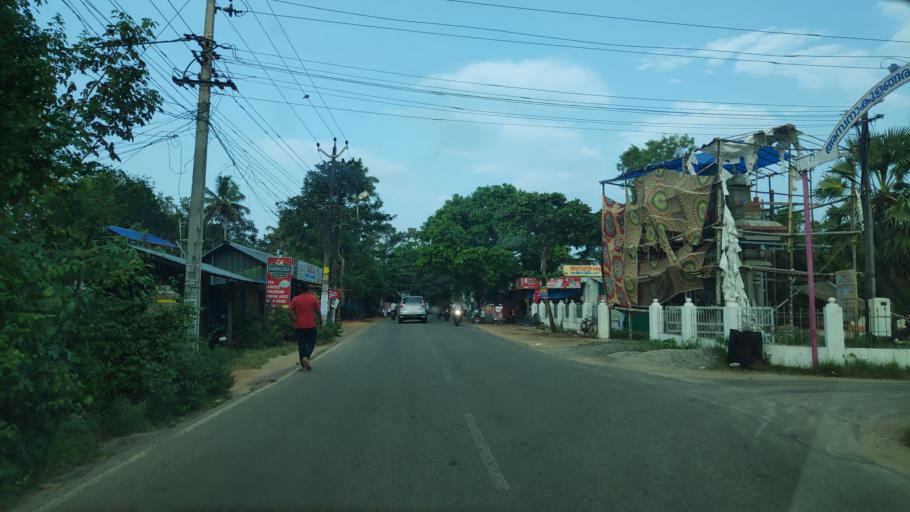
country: IN
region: Kerala
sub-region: Alappuzha
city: Alleppey
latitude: 9.5642
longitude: 76.3462
